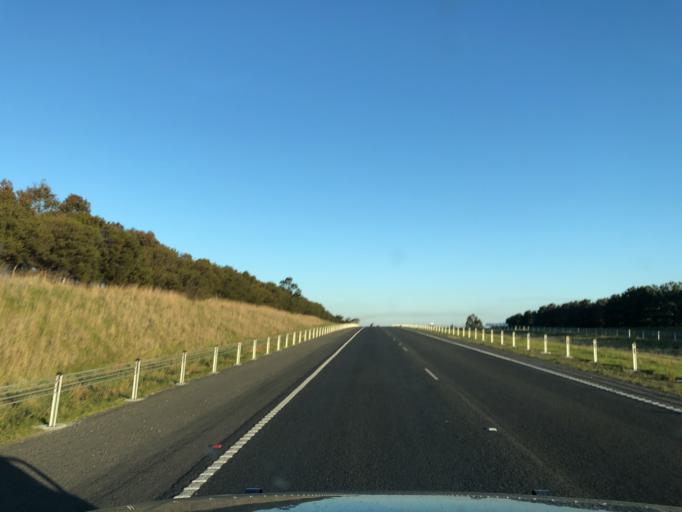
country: AU
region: Victoria
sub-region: Moorabool
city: Bacchus Marsh
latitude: -37.6222
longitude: 144.3416
